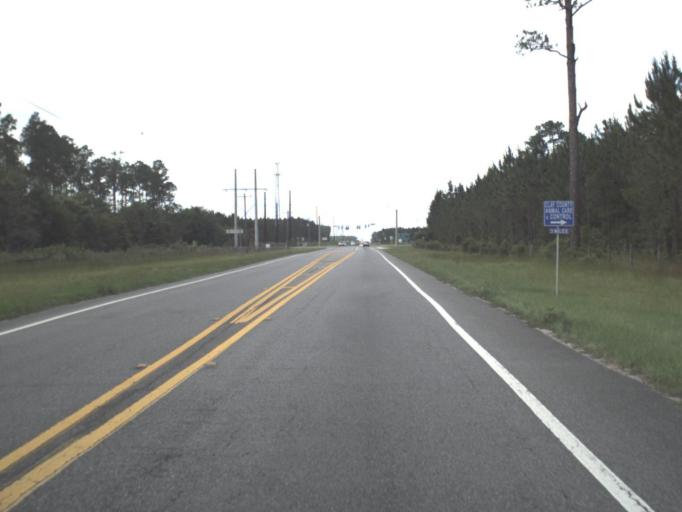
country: US
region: Florida
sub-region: Clay County
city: Middleburg
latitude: 29.9756
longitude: -81.8977
